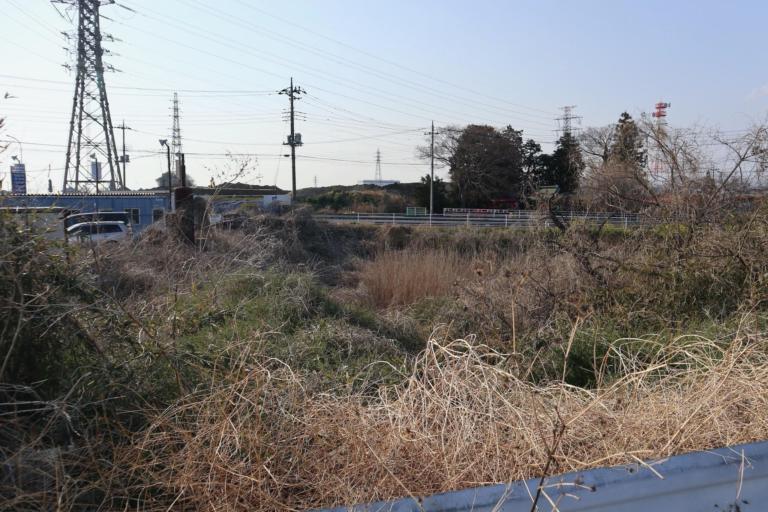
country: JP
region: Gunma
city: Tatebayashi
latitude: 36.2774
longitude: 139.5571
